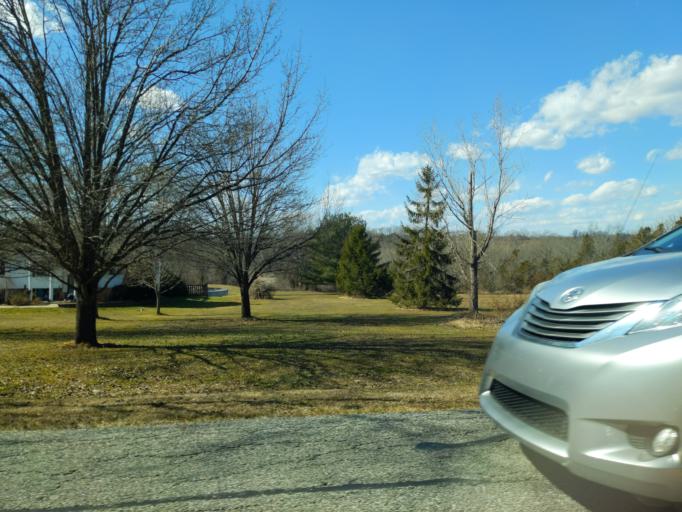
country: US
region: Pennsylvania
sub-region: Montgomery County
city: Red Hill
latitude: 40.3513
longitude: -75.4641
